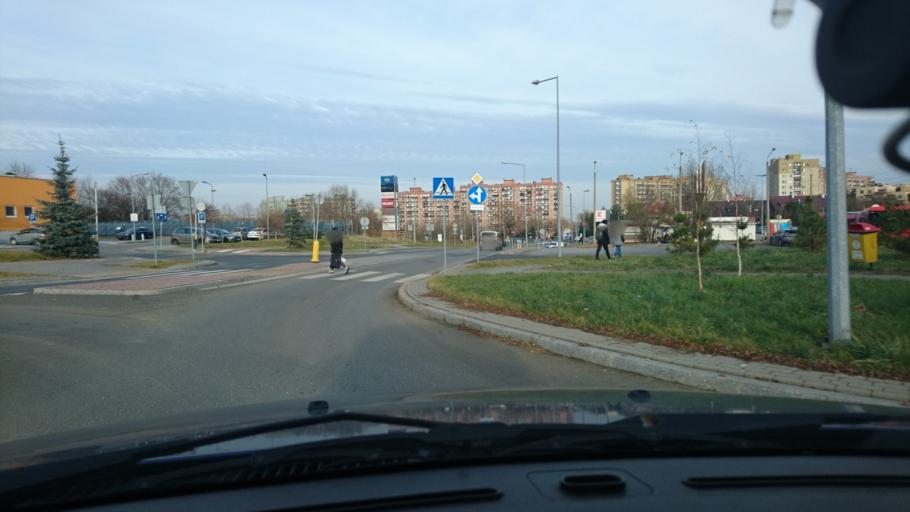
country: PL
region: Silesian Voivodeship
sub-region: Bielsko-Biala
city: Bielsko-Biala
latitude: 49.8004
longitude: 19.0296
